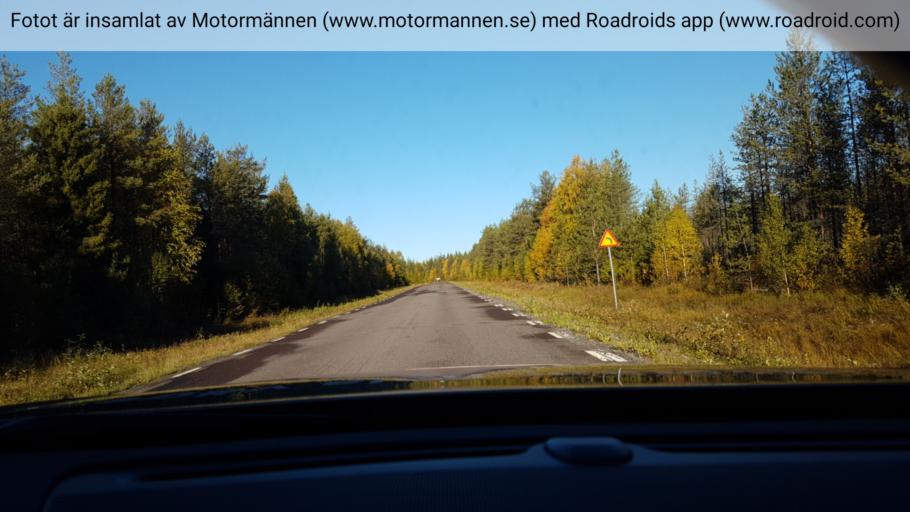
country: SE
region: Norrbotten
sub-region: Bodens Kommun
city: Boden
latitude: 66.0585
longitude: 21.4328
